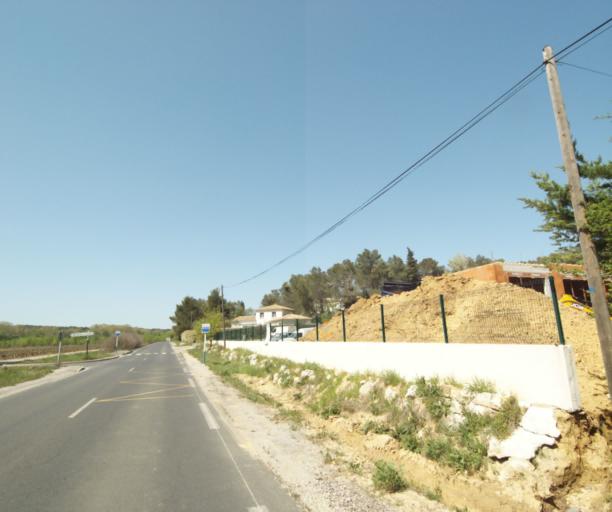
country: FR
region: Languedoc-Roussillon
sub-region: Departement de l'Herault
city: Montferrier-sur-Lez
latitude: 43.6598
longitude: 3.8493
